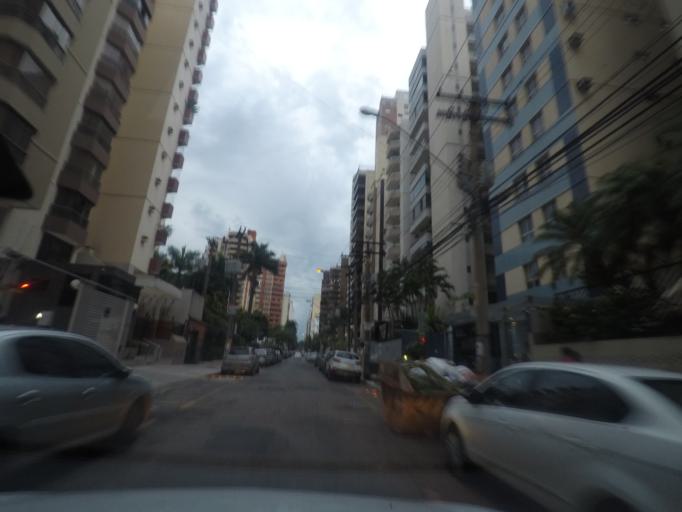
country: BR
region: Goias
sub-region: Goiania
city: Goiania
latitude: -16.7112
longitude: -49.2661
